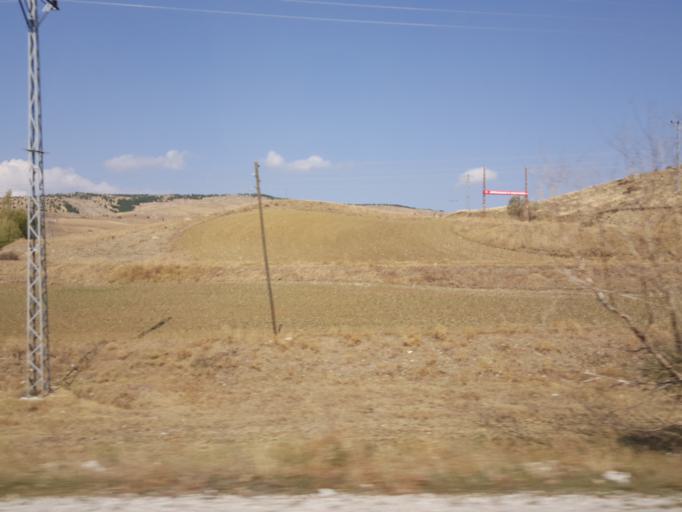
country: TR
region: Corum
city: Bogazkale
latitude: 40.1594
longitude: 34.6331
